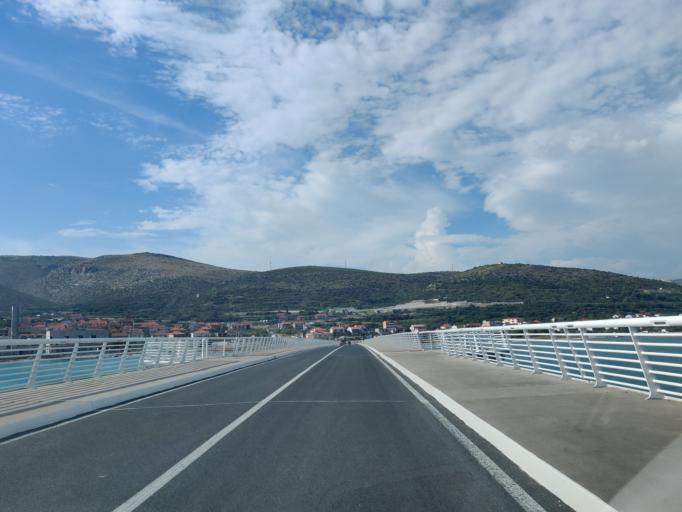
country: HR
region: Splitsko-Dalmatinska
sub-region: Grad Trogir
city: Trogir
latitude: 43.5181
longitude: 16.2650
